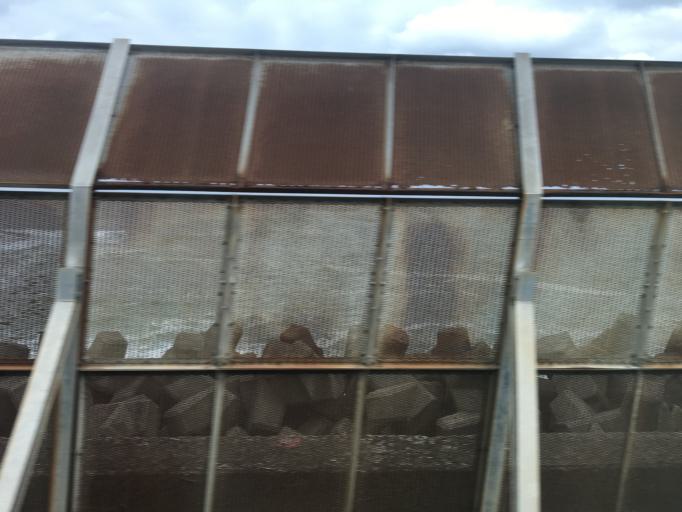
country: JP
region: Aomori
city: Shimokizukuri
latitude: 40.6732
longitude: 139.9542
